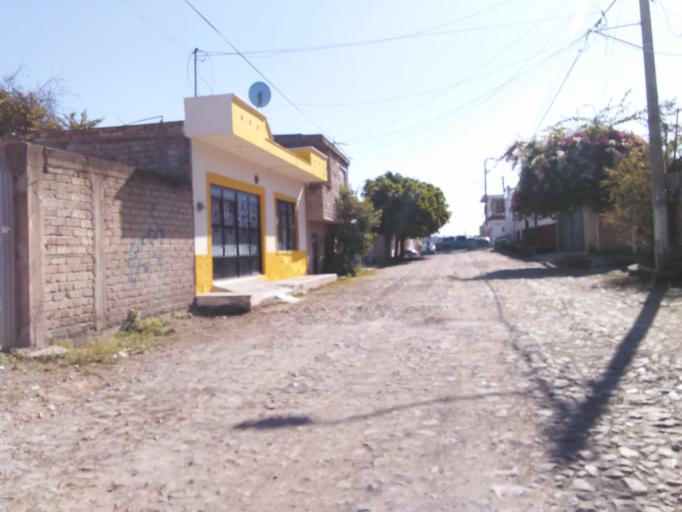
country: MX
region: Nayarit
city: Tepic
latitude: 21.5262
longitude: -104.9223
